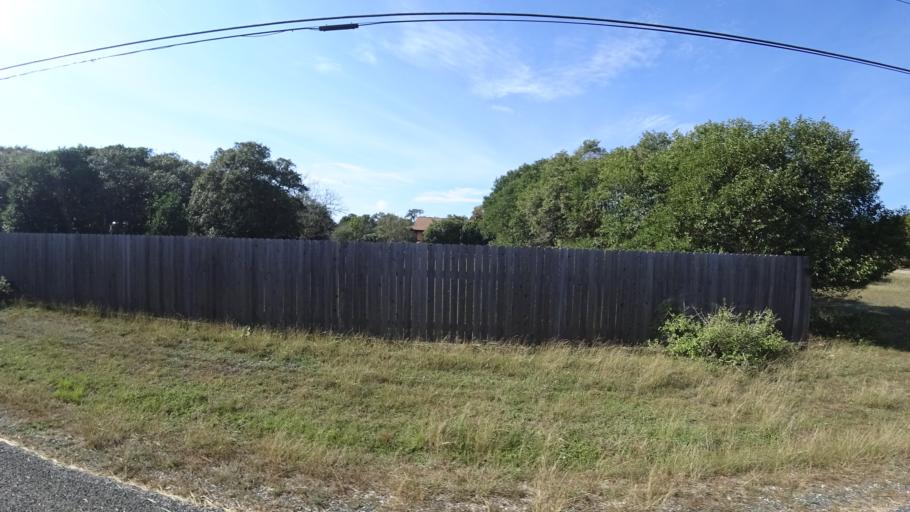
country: US
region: Texas
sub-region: Travis County
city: Barton Creek
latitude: 30.2278
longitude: -97.9095
